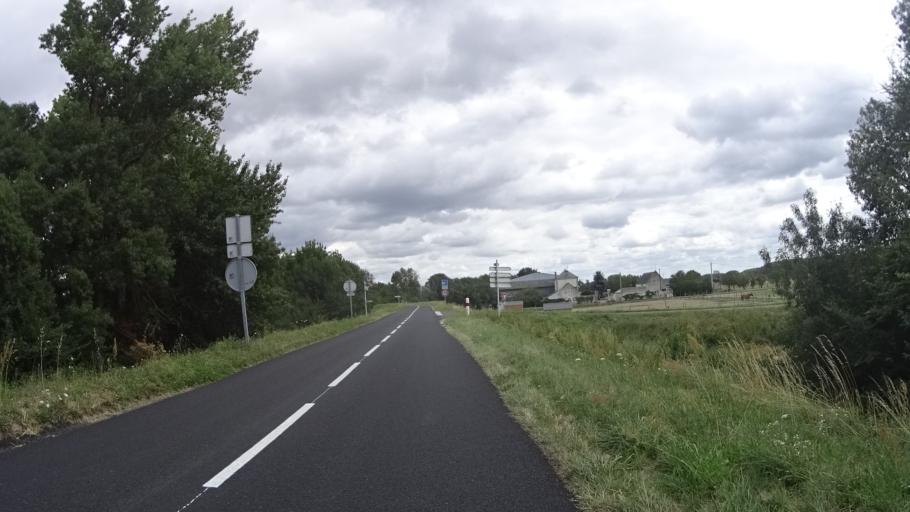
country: FR
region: Centre
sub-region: Departement d'Indre-et-Loire
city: Huismes
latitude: 47.2665
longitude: 0.3080
